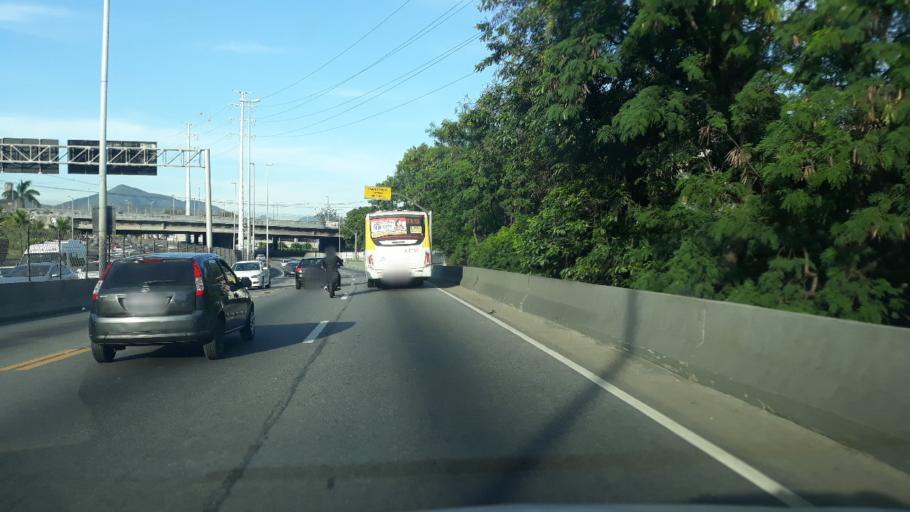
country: BR
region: Rio de Janeiro
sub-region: Rio De Janeiro
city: Rio de Janeiro
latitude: -22.8758
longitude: -43.2742
